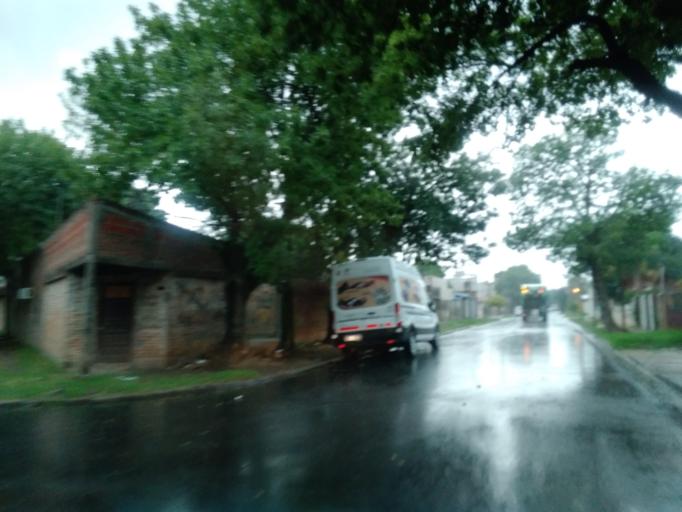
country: AR
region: Corrientes
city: Corrientes
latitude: -27.4906
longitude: -58.8222
